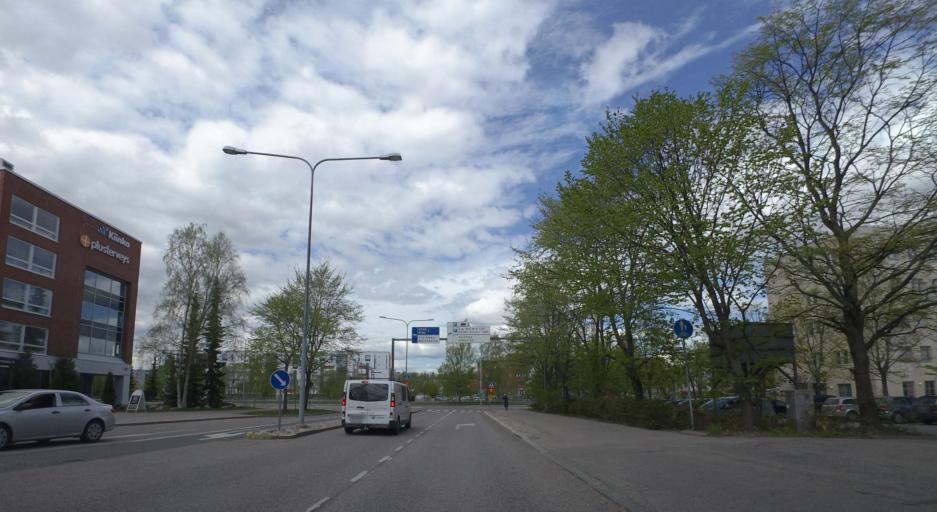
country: FI
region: Uusimaa
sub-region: Helsinki
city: Vantaa
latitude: 60.2483
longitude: 25.0081
